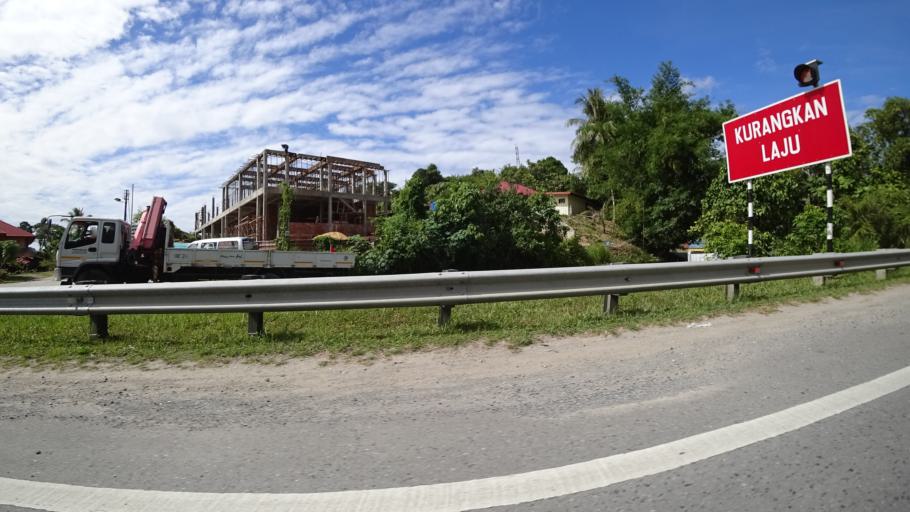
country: BN
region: Brunei and Muara
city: Bandar Seri Begawan
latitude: 4.8797
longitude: 114.8738
